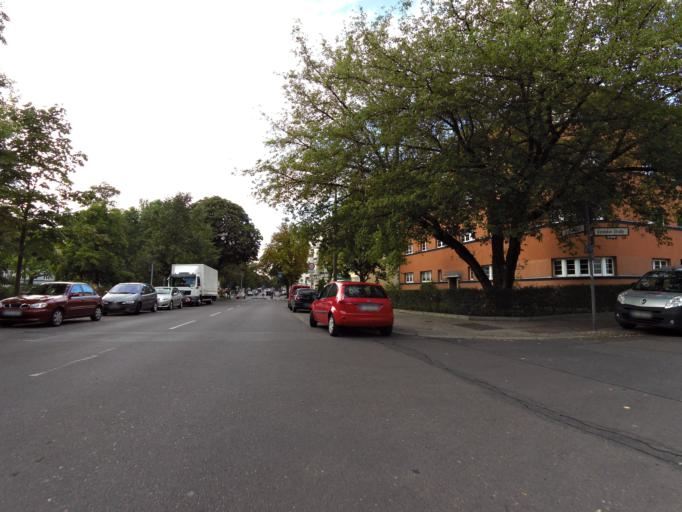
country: DE
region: Berlin
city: Baumschulenweg
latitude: 52.4636
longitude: 13.4899
